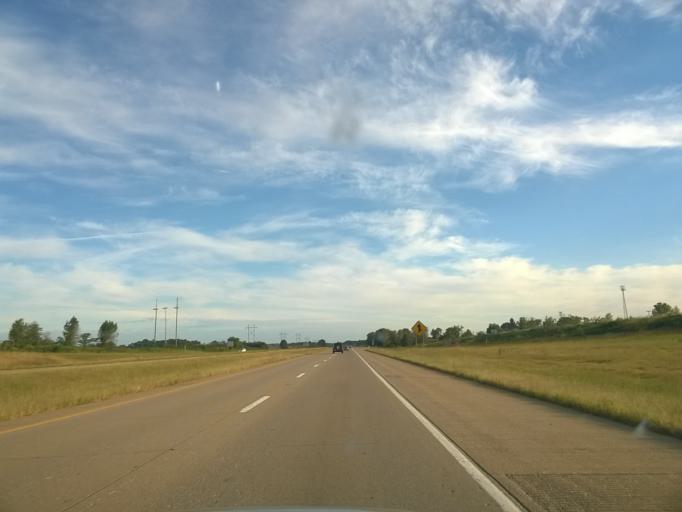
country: US
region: Indiana
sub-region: Vanderburgh County
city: Melody Hill
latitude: 38.0917
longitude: -87.4764
